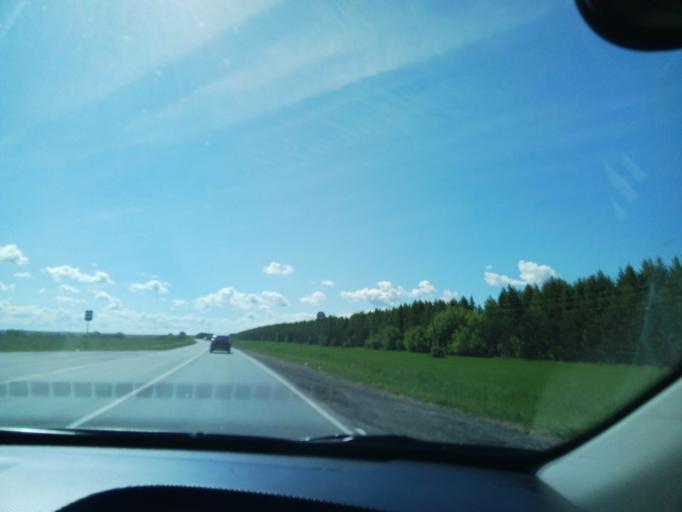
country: RU
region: Chuvashia
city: Atlashevo
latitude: 56.0489
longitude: 47.5198
